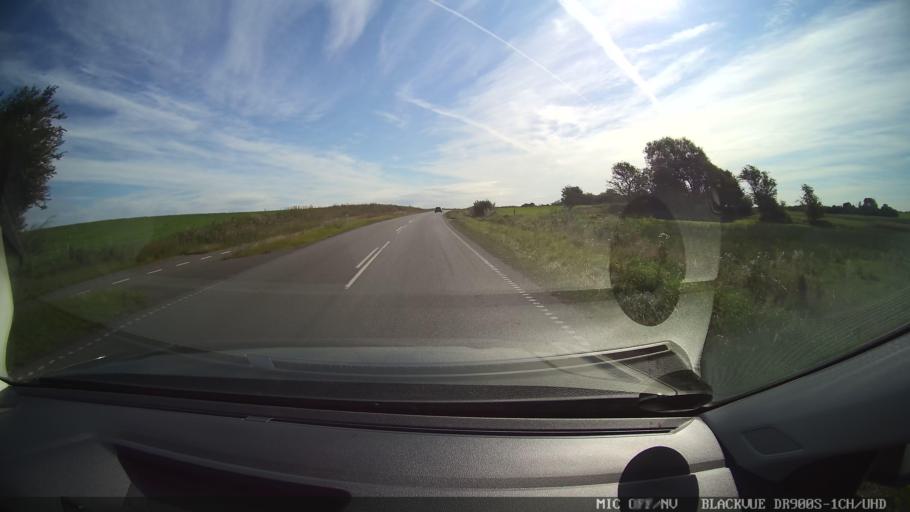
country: DK
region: North Denmark
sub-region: Mariagerfjord Kommune
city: Arden
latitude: 56.7651
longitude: 9.8966
